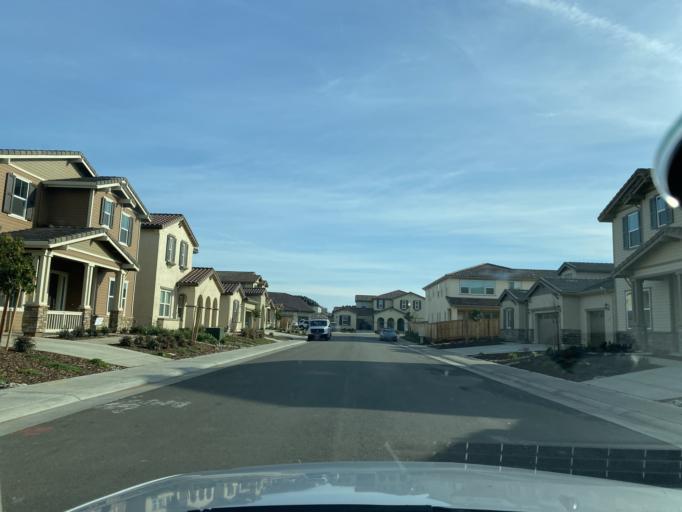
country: US
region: California
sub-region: Sacramento County
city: Elk Grove
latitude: 38.3939
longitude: -121.3868
